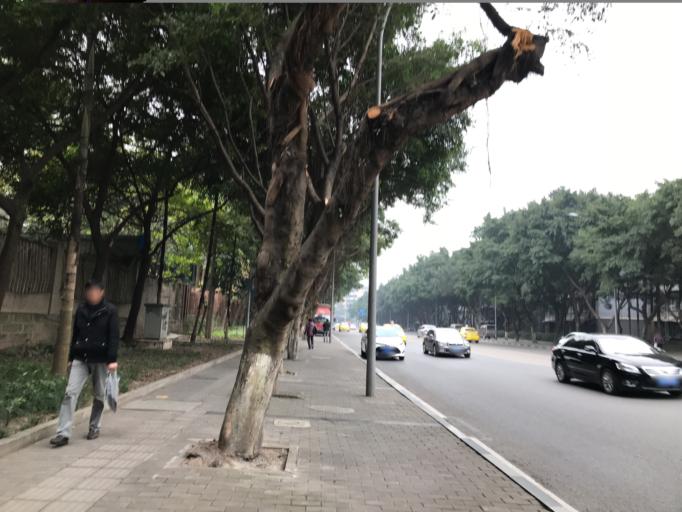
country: CN
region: Chongqing Shi
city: Chongqing
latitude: 29.5268
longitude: 106.5480
